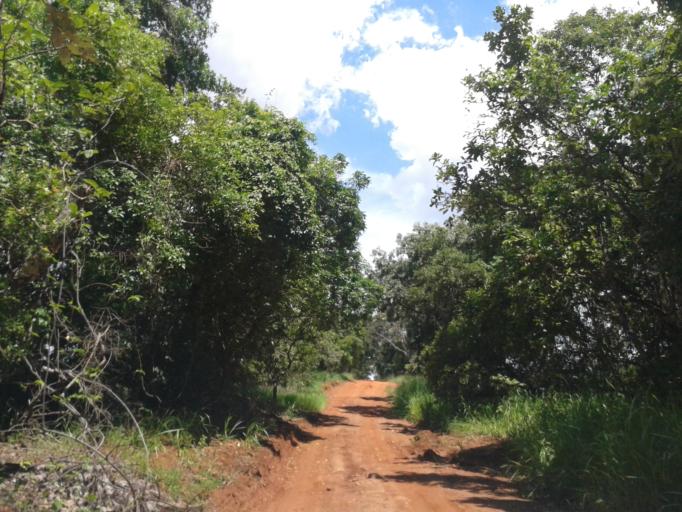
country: BR
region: Minas Gerais
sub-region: Ituiutaba
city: Ituiutaba
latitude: -18.8581
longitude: -49.4982
